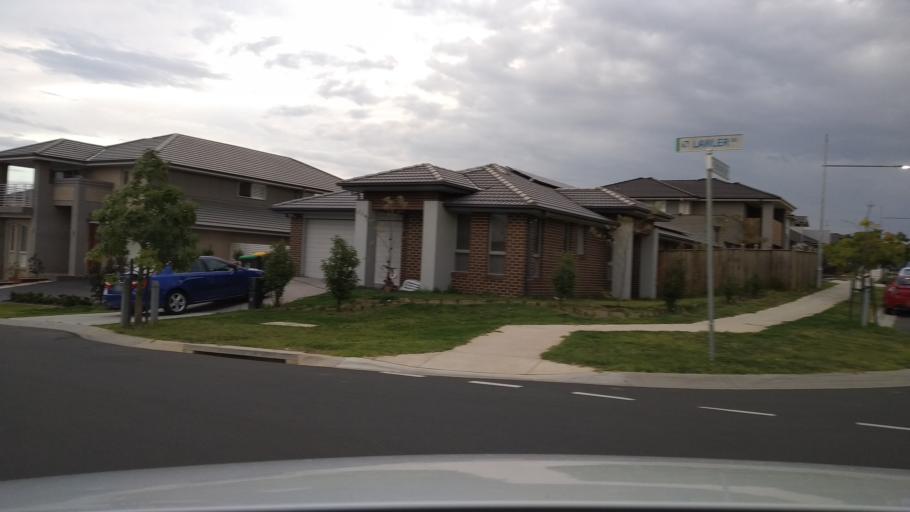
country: AU
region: New South Wales
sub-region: Camden
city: Narellan
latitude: -34.0043
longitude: 150.7260
